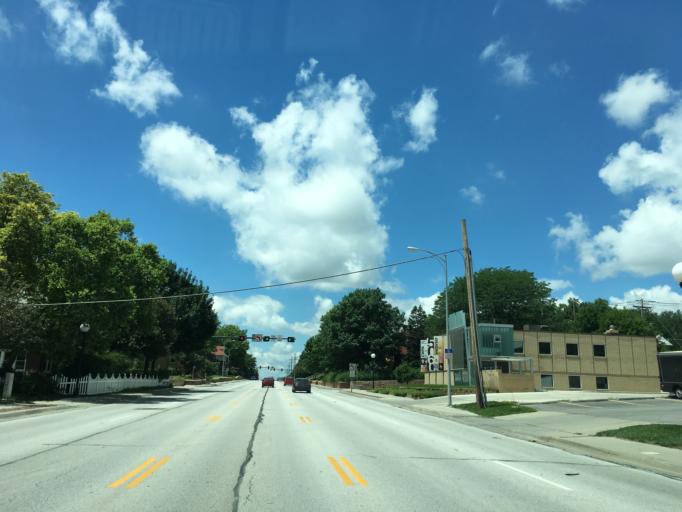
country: US
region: Nebraska
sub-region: Douglas County
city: Omaha
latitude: 41.2596
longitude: -95.9915
